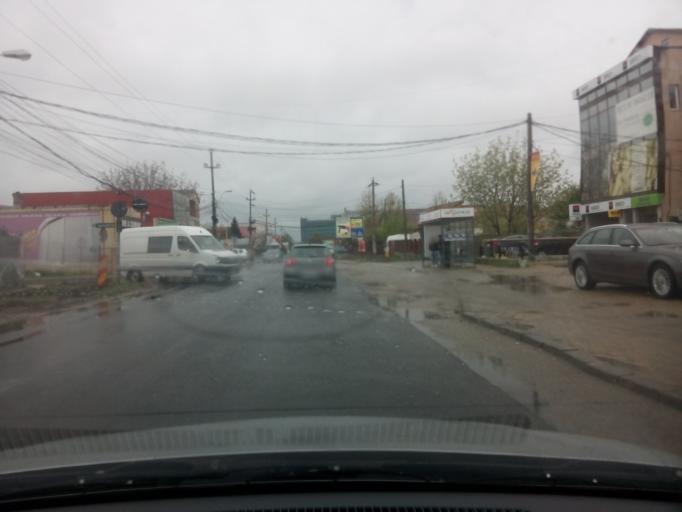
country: RO
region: Ilfov
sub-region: Voluntari City
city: Voluntari
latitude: 44.5031
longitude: 26.1357
